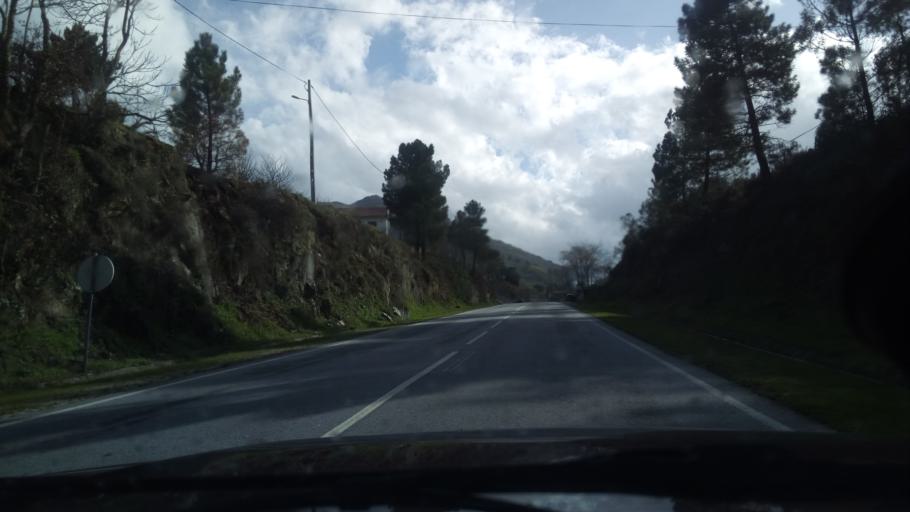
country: PT
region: Guarda
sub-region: Guarda
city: Guarda
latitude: 40.5922
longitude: -7.2896
